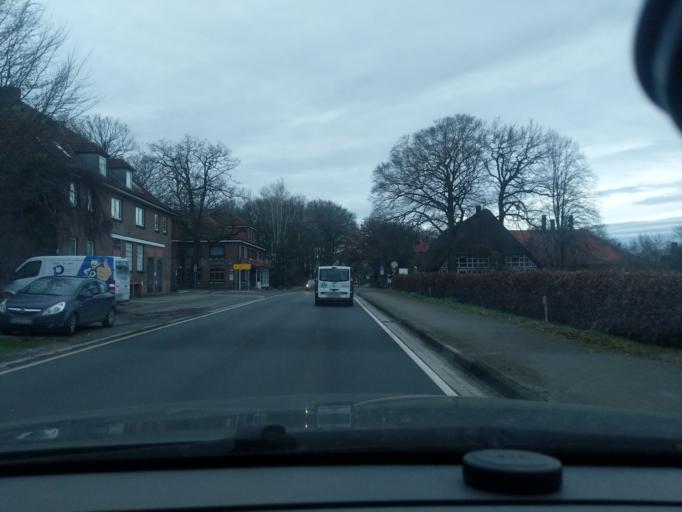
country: DE
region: Lower Saxony
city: Sauensiek
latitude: 53.3788
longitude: 9.5959
